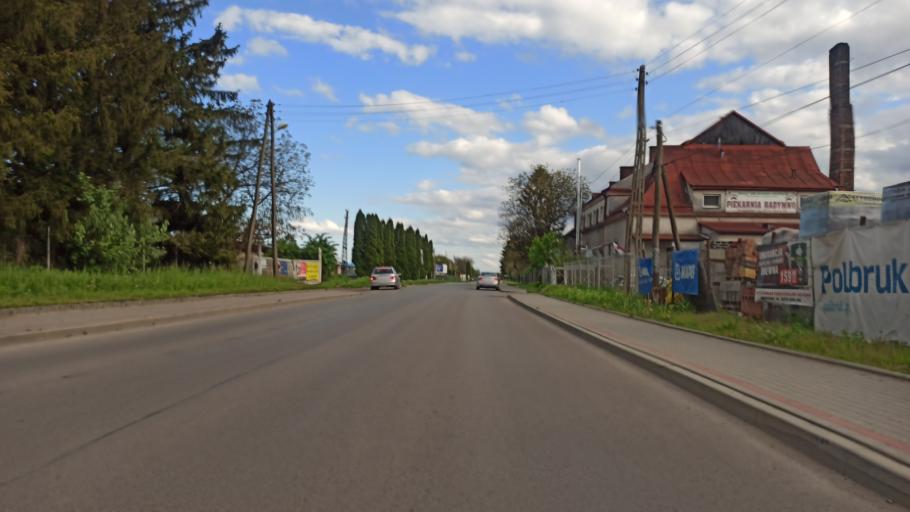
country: PL
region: Subcarpathian Voivodeship
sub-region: Powiat jaroslawski
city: Radymno
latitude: 49.9402
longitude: 22.8323
